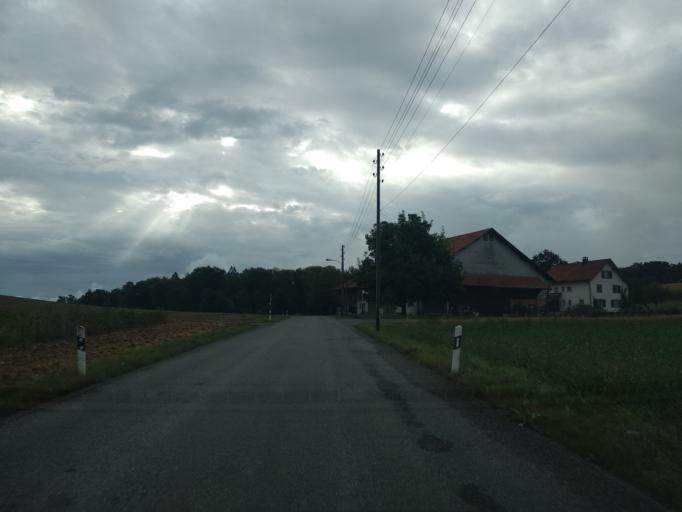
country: CH
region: Zurich
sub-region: Bezirk Andelfingen
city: Marthalen
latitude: 47.6511
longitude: 8.6841
